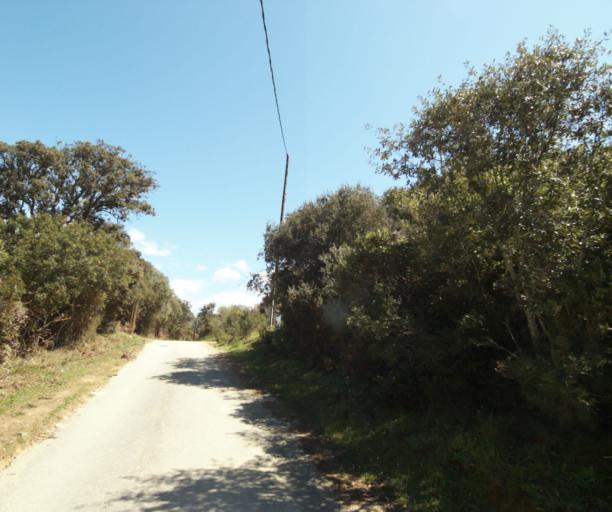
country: FR
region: Corsica
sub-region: Departement de la Corse-du-Sud
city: Propriano
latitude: 41.6413
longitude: 8.8696
